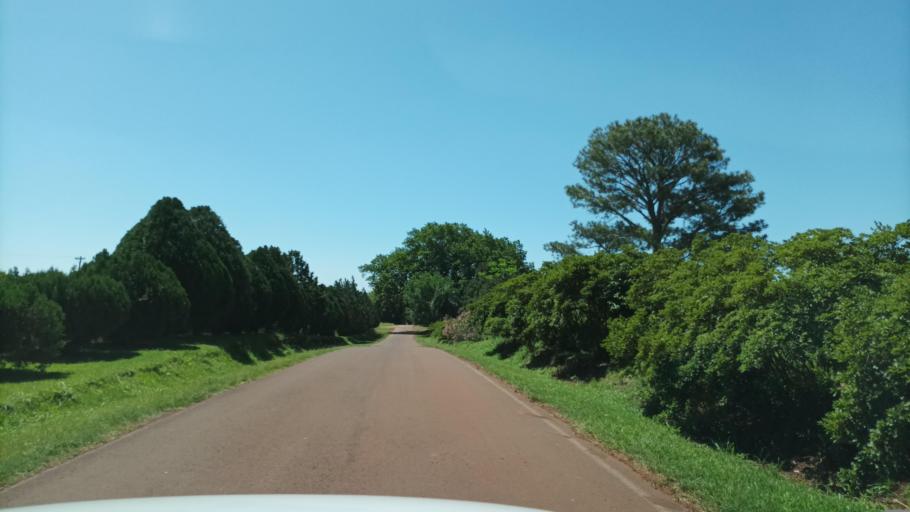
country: AR
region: Misiones
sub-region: Departamento de Apostoles
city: San Jose
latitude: -27.7908
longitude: -55.7161
